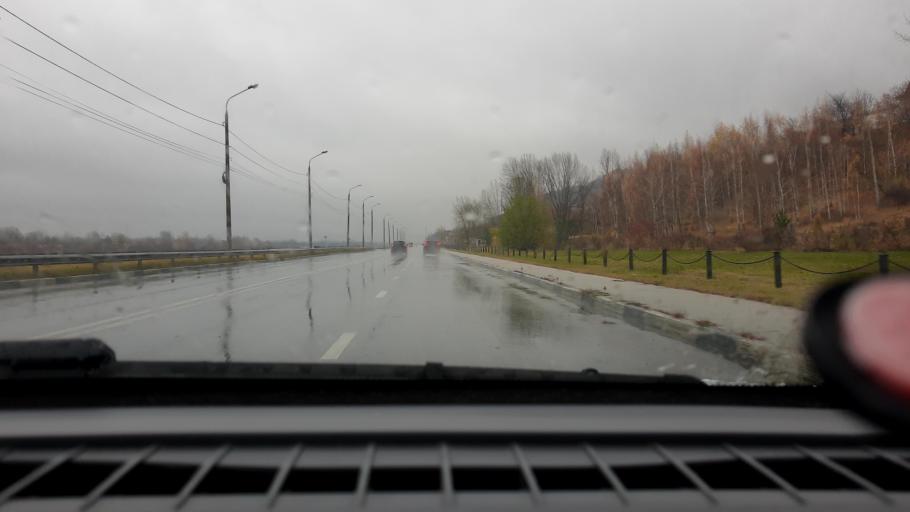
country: RU
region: Nizjnij Novgorod
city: Bor
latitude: 56.3256
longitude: 44.0493
